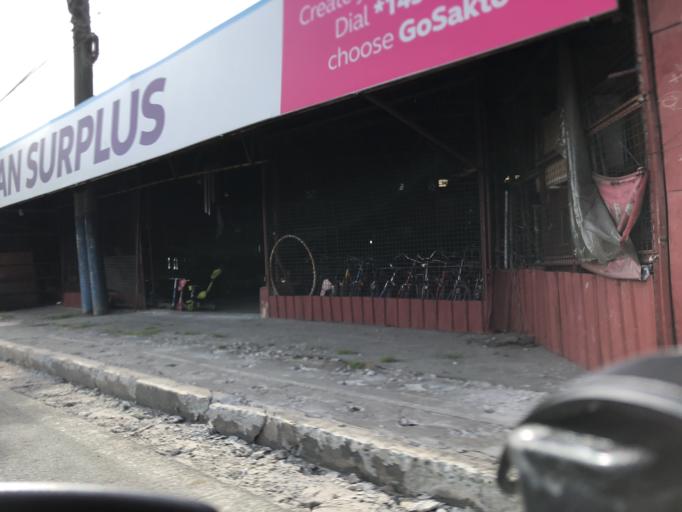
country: PH
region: Calabarzon
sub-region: Province of Rizal
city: San Mateo
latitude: 14.7285
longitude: 121.0609
